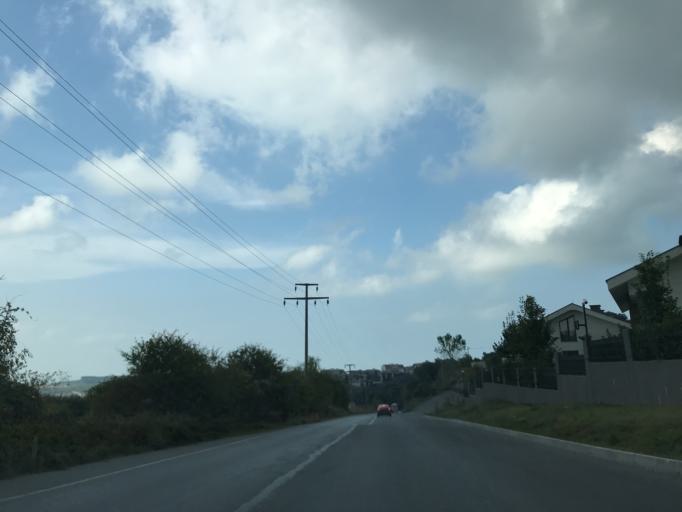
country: TR
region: Istanbul
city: Arikoey
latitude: 41.2069
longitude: 29.0404
